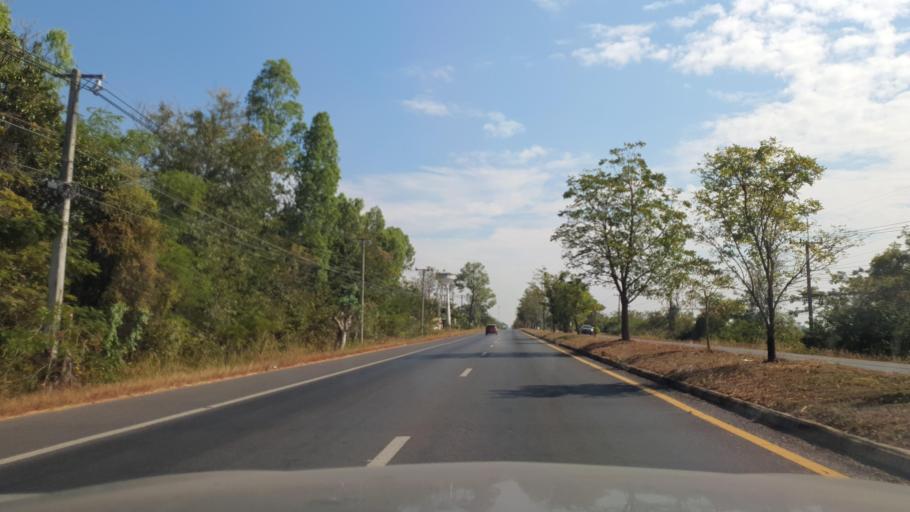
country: TH
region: Maha Sarakham
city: Kantharawichai
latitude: 16.3880
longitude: 103.2551
